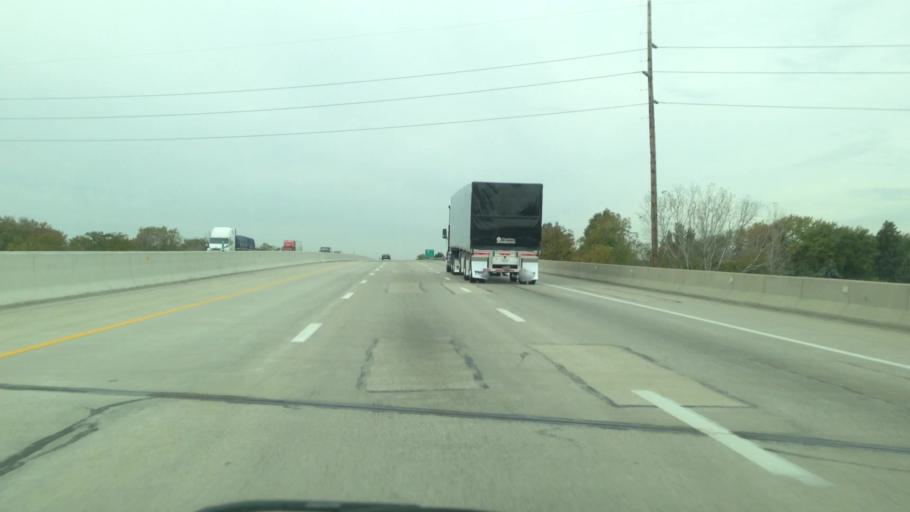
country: US
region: Ohio
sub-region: Wood County
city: Perrysburg
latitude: 41.5881
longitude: -83.6311
